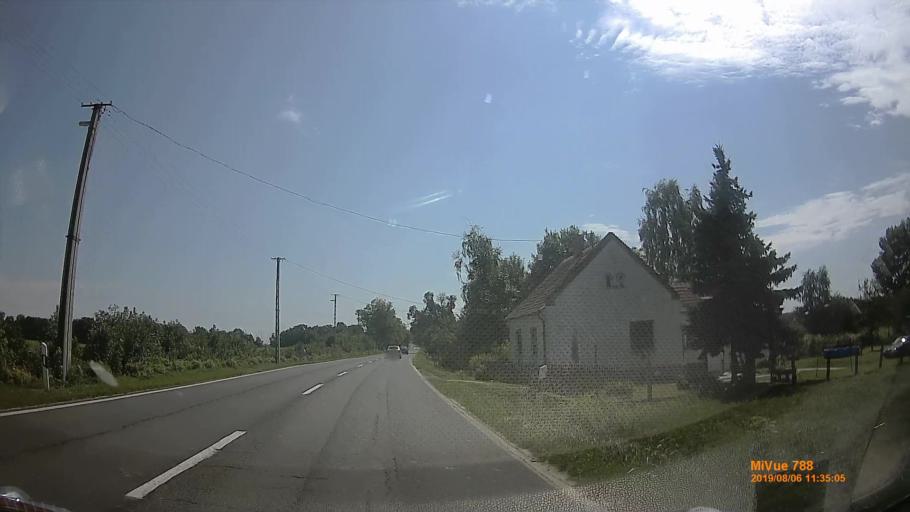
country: AT
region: Burgenland
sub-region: Politischer Bezirk Gussing
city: Heiligenbrunn
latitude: 46.9692
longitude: 16.4200
